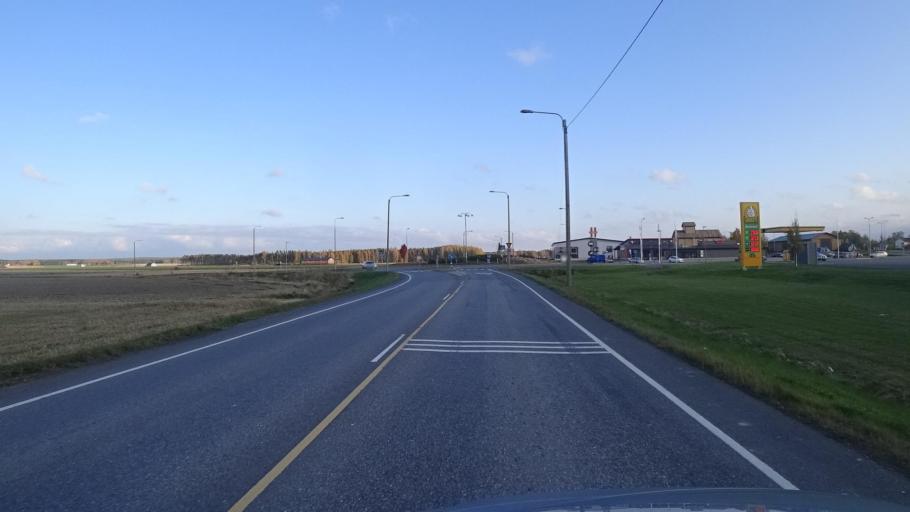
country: FI
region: Satakunta
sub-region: Rauma
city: Saekylae
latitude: 61.0471
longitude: 22.3573
